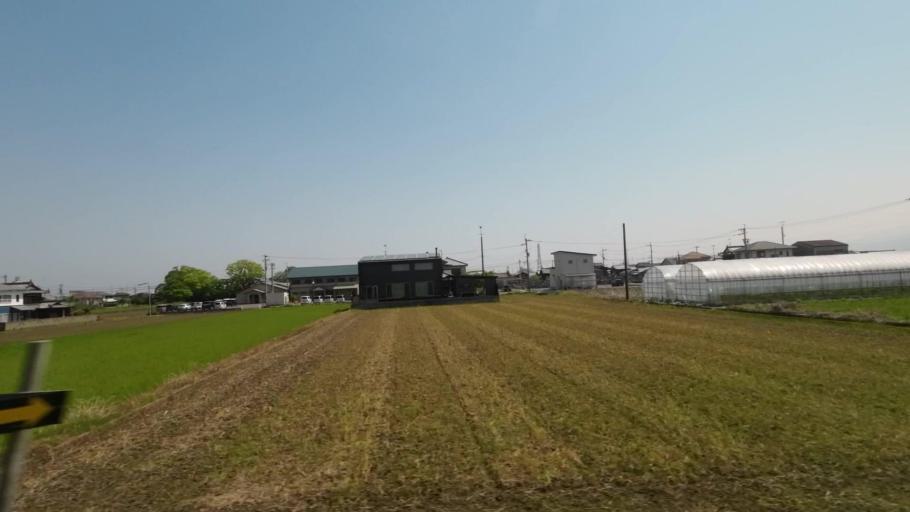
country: JP
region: Ehime
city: Saijo
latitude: 33.9244
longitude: 133.0903
